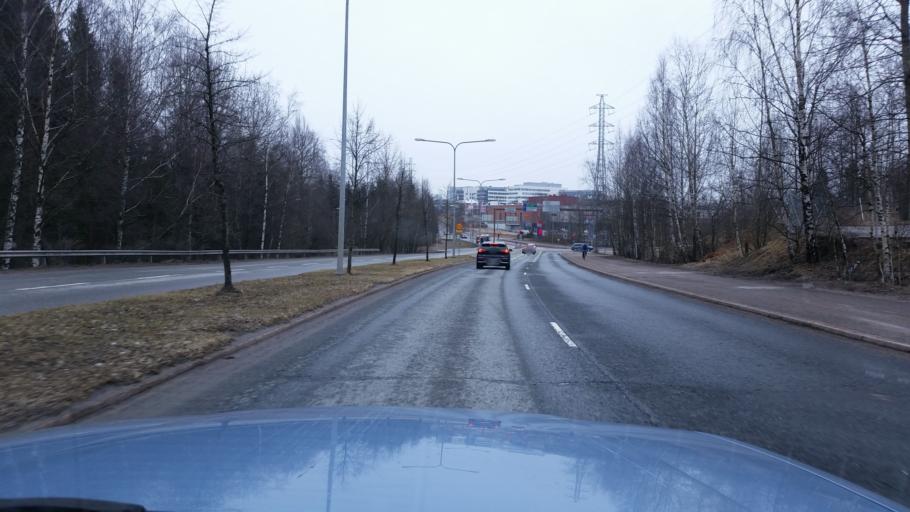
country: FI
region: Uusimaa
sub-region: Helsinki
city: Helsinki
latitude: 60.2208
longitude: 24.9302
